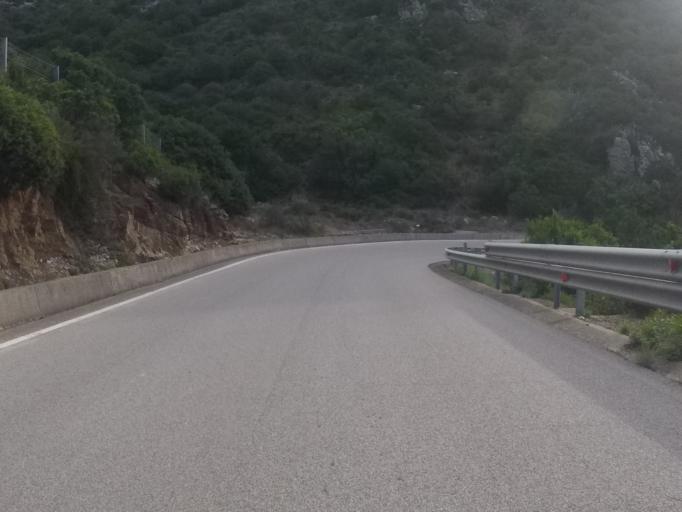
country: IT
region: Sardinia
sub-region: Provincia di Carbonia-Iglesias
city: Gonnesa
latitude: 39.3332
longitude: 8.4416
